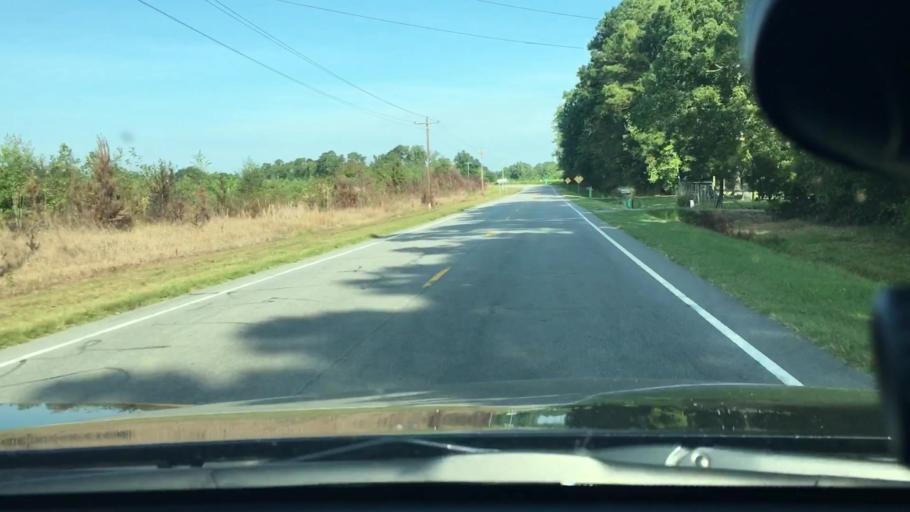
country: US
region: North Carolina
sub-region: Edgecombe County
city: Pinetops
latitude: 35.7870
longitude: -77.6227
